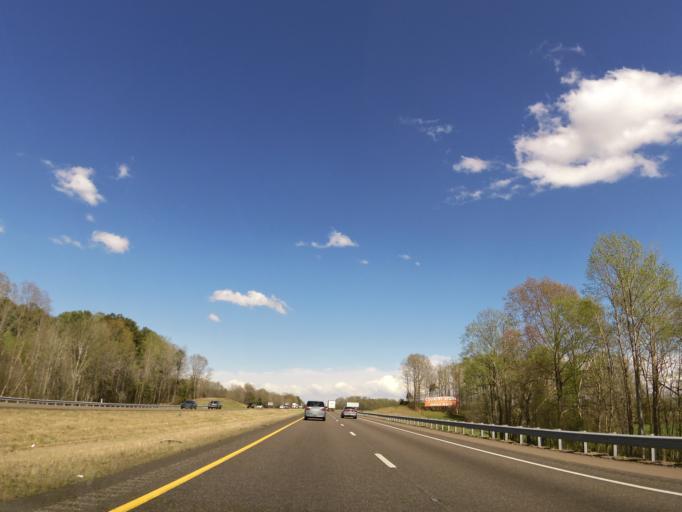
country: US
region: Tennessee
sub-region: Henderson County
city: Lexington
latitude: 35.7603
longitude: -88.4880
